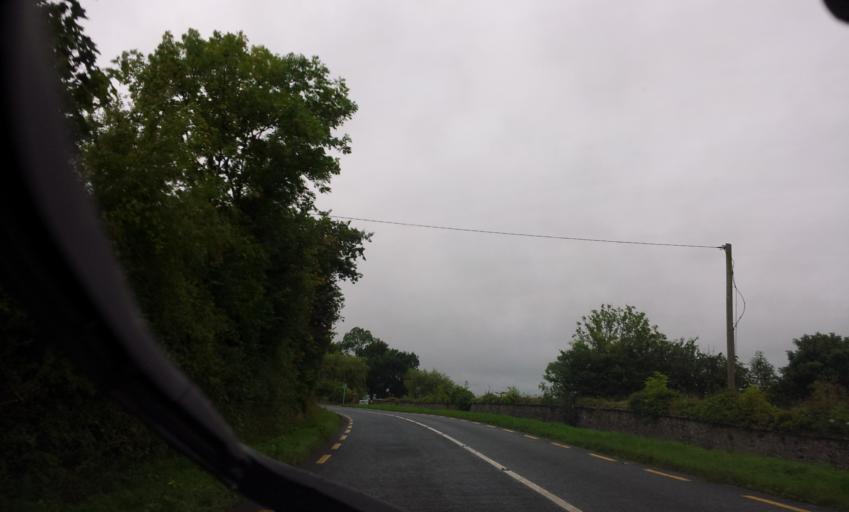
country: IE
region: Munster
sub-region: County Cork
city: Mitchelstown
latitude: 52.2656
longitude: -8.2938
